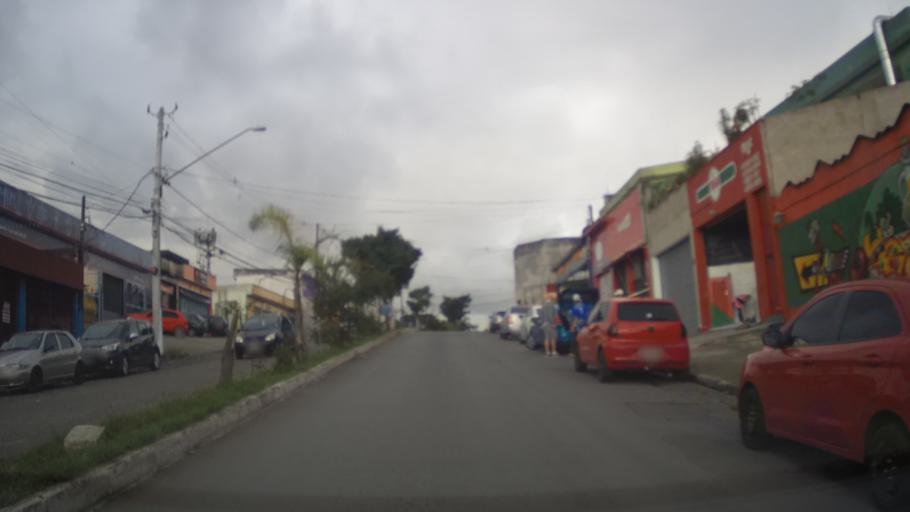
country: BR
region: Sao Paulo
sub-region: Itaquaquecetuba
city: Itaquaquecetuba
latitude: -23.4454
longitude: -46.4149
